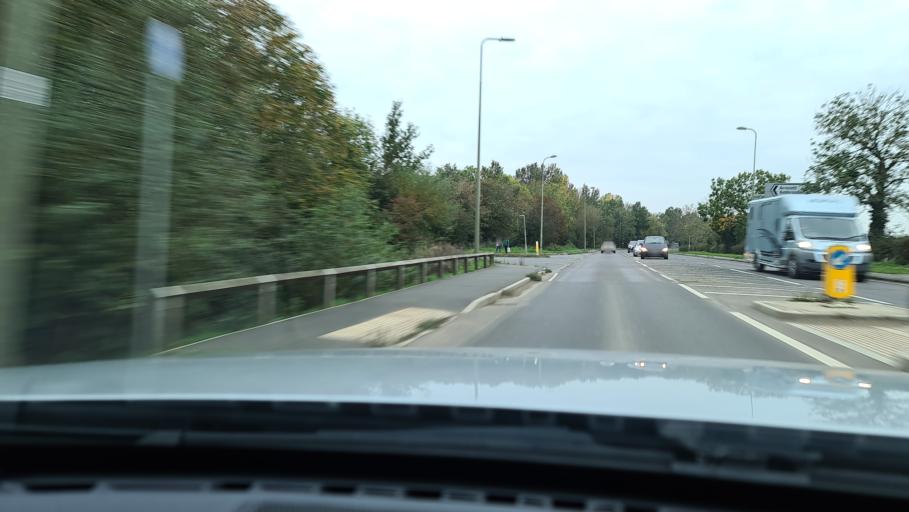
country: GB
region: England
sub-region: Oxfordshire
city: Bicester
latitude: 51.8801
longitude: -1.1283
